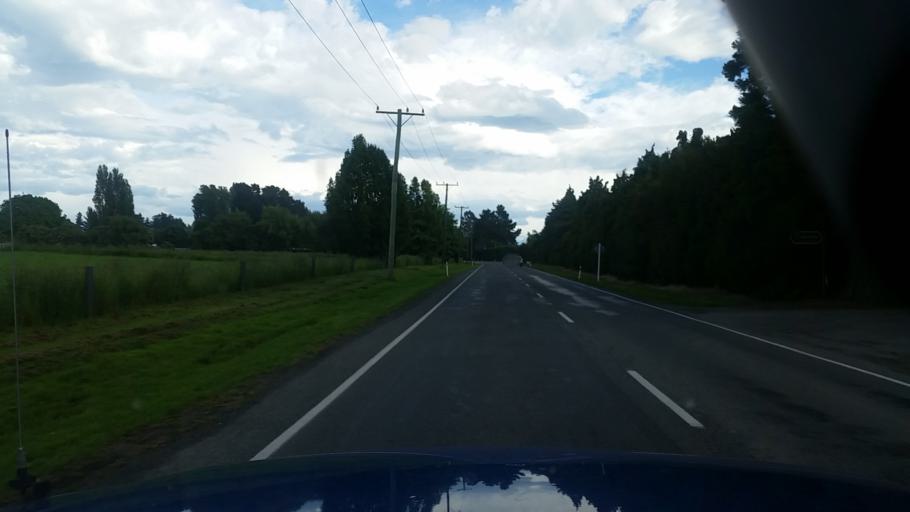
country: NZ
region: Canterbury
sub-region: Ashburton District
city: Ashburton
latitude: -43.8804
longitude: 171.7312
